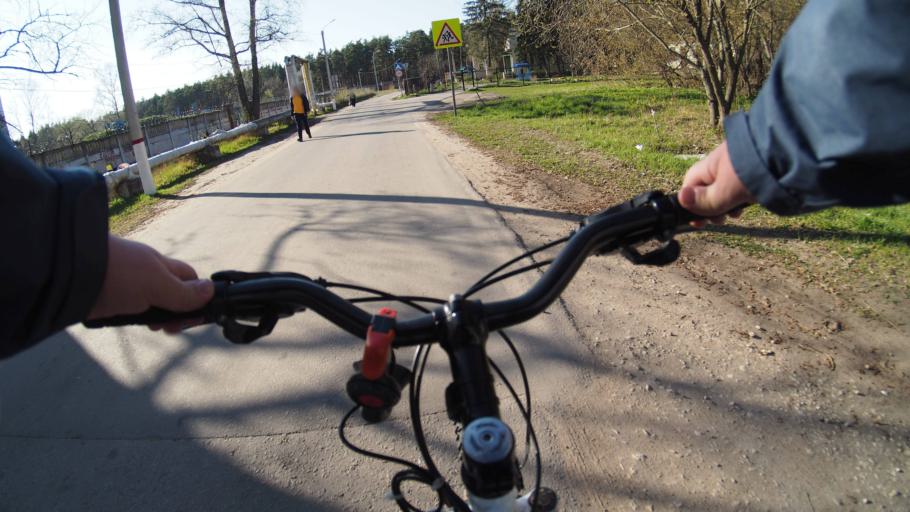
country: RU
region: Moskovskaya
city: Malyshevo
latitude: 55.5114
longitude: 38.3354
